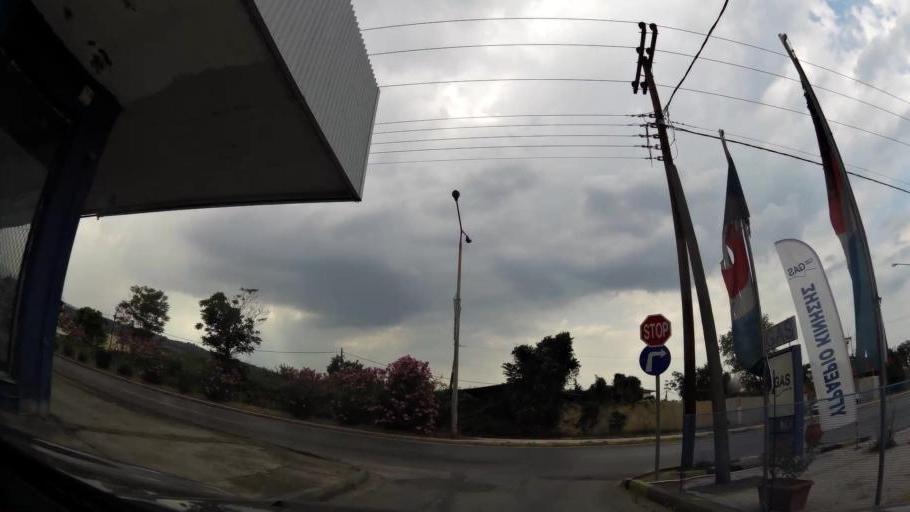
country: GR
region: Central Macedonia
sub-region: Nomos Imathias
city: Veroia
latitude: 40.5340
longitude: 22.2089
